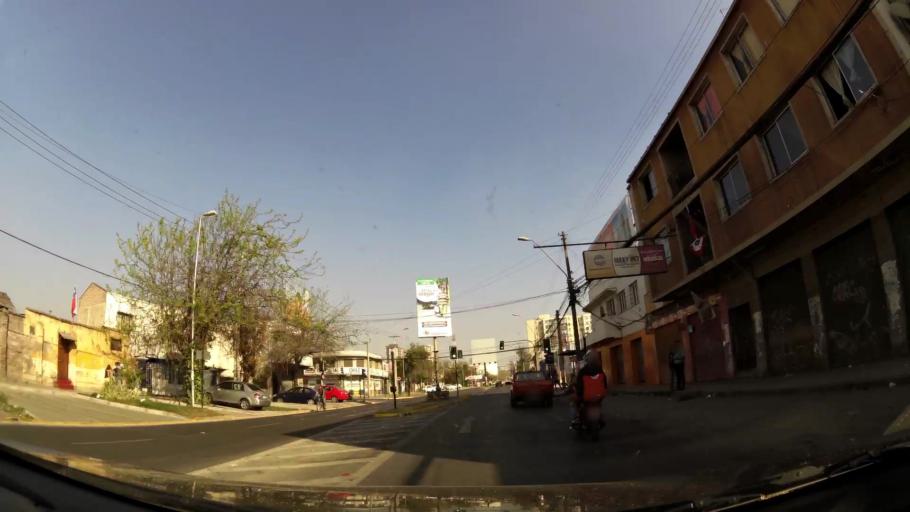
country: CL
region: Santiago Metropolitan
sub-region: Provincia de Santiago
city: Santiago
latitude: -33.4152
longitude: -70.6645
